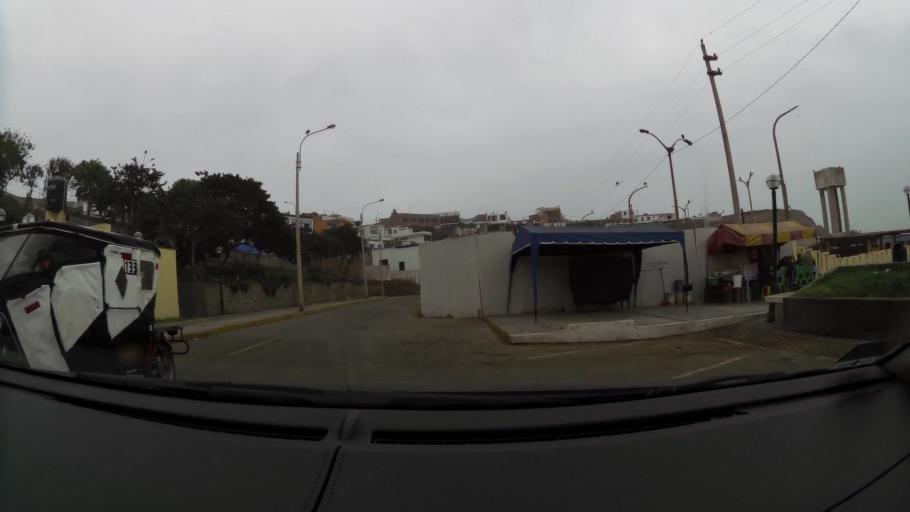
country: PE
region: Lima
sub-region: Provincia de Huaral
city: Chancay
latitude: -11.5857
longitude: -77.2728
